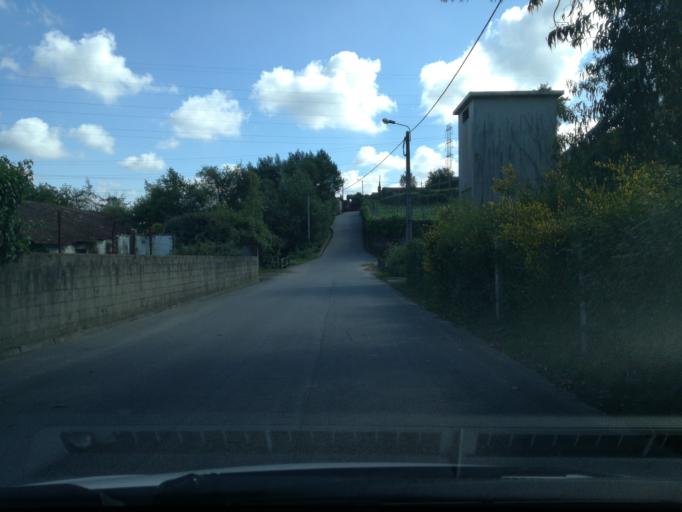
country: PT
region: Porto
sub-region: Valongo
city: Ermesinde
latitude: 41.2397
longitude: -8.5574
